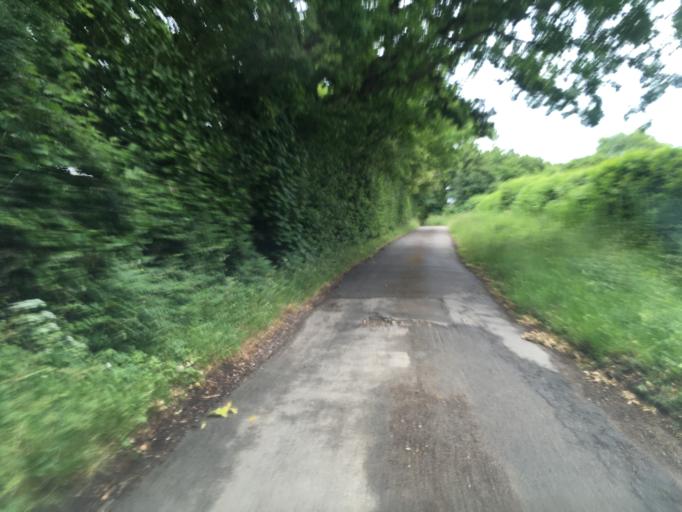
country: GB
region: England
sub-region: Gloucestershire
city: Shurdington
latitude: 51.8040
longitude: -2.0833
